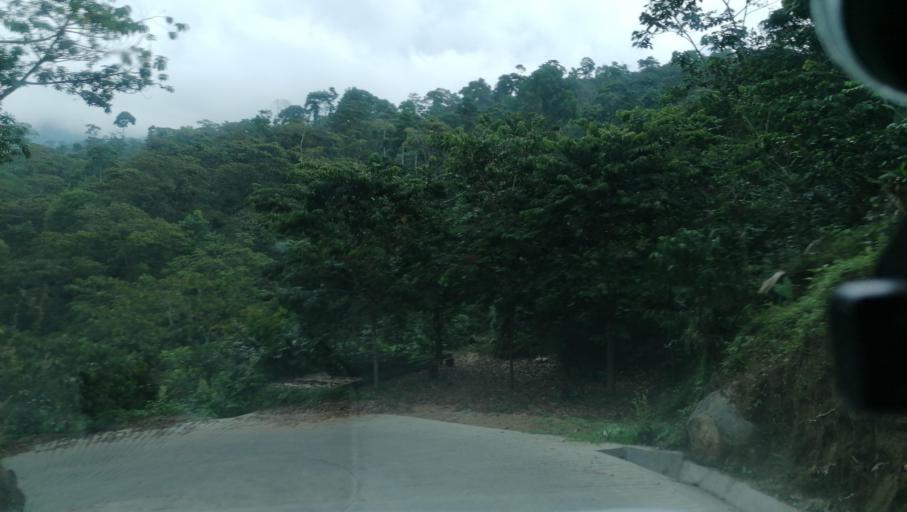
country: MX
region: Chiapas
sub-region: Cacahoatan
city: Benito Juarez
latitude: 15.0733
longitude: -92.1656
